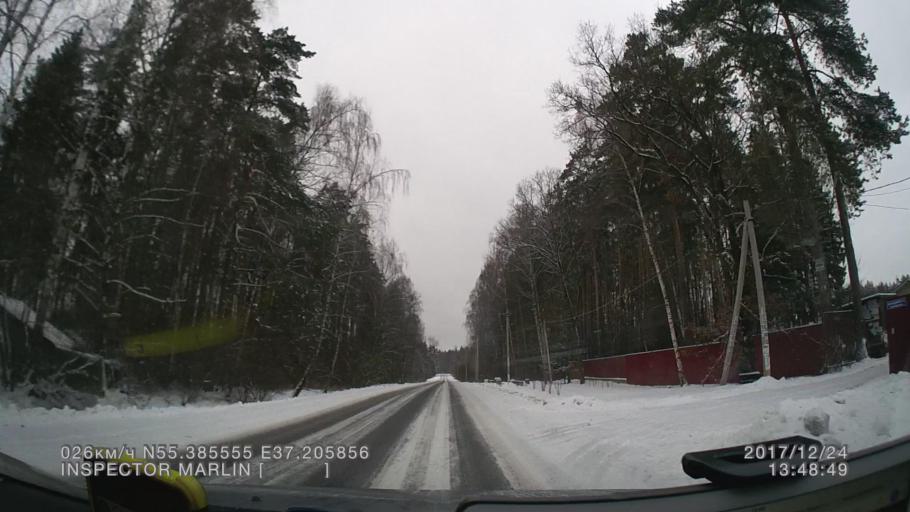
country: RU
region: Moskovskaya
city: Troitsk
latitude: 55.3856
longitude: 37.2059
